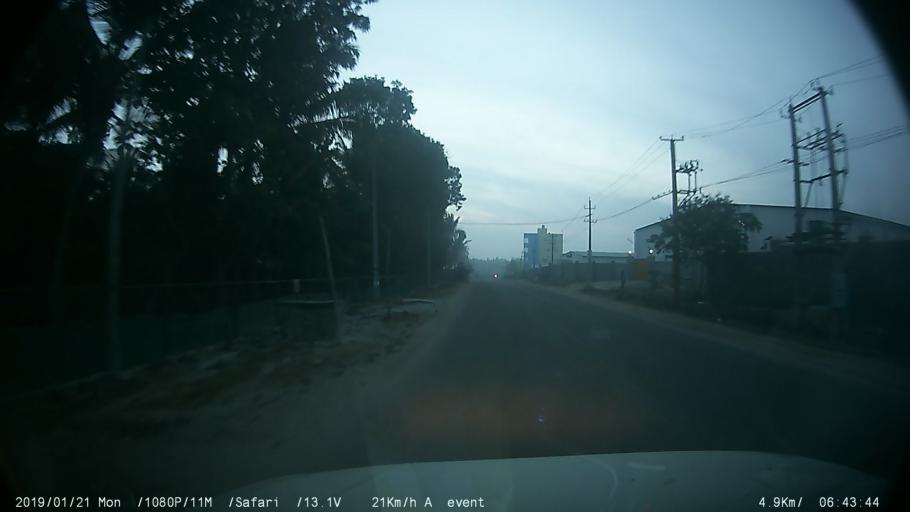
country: IN
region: Karnataka
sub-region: Bangalore Urban
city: Anekal
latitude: 12.8208
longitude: 77.6233
